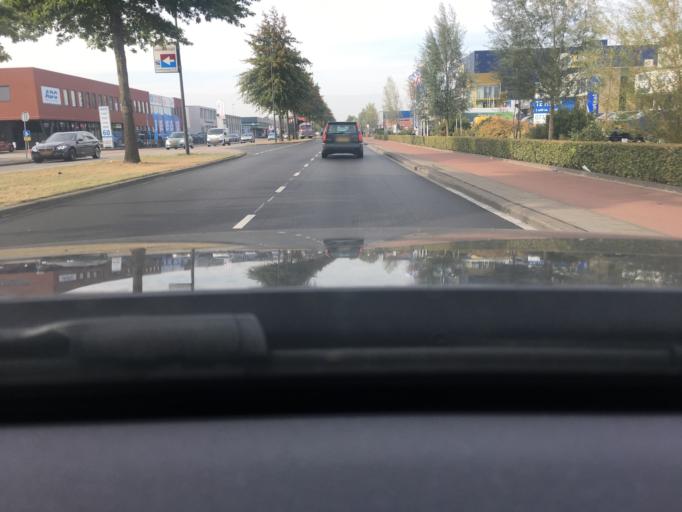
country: NL
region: North Brabant
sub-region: Gemeente 's-Hertogenbosch
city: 's-Hertogenbosch
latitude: 51.7032
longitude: 5.2715
